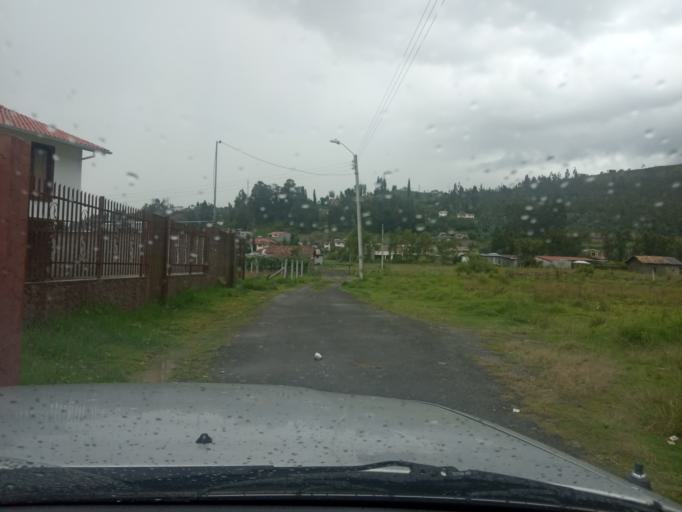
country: EC
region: Azuay
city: Llacao
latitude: -2.8675
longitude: -78.9439
